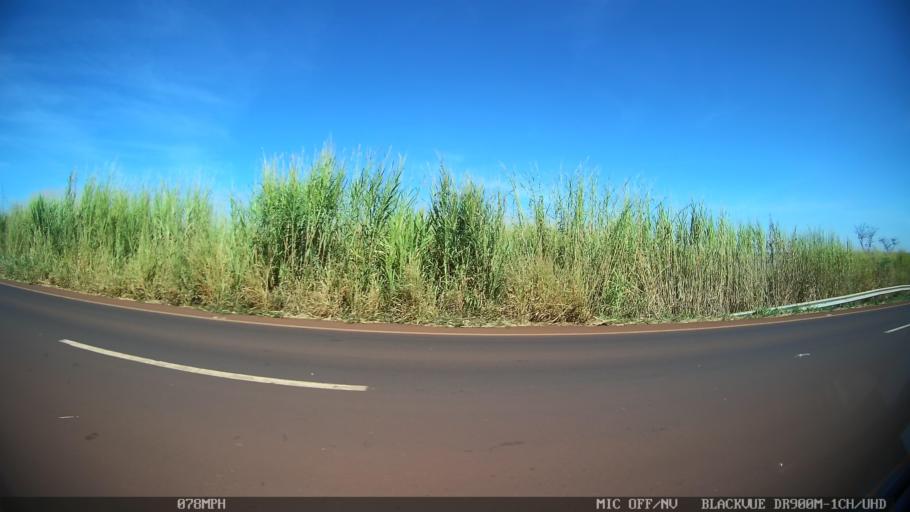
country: BR
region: Sao Paulo
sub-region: Sao Joaquim Da Barra
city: Sao Joaquim da Barra
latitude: -20.5419
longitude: -47.8014
